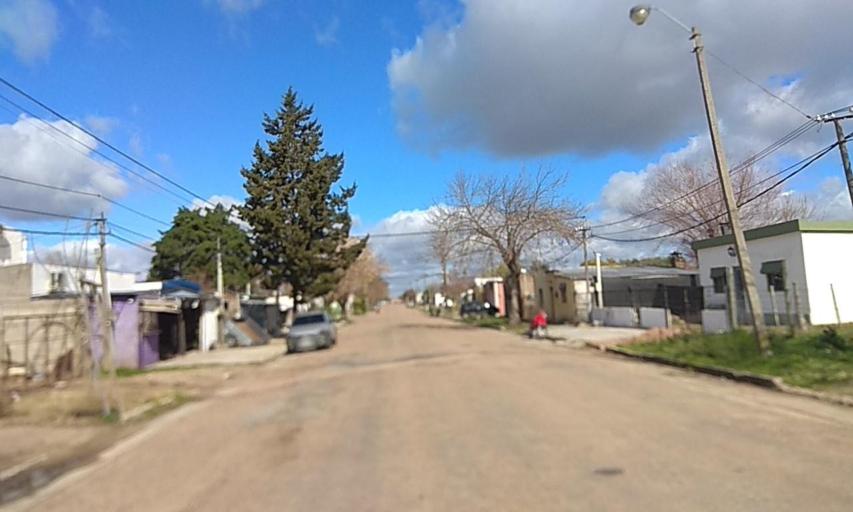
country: UY
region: Florida
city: Florida
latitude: -34.0816
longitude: -56.2218
